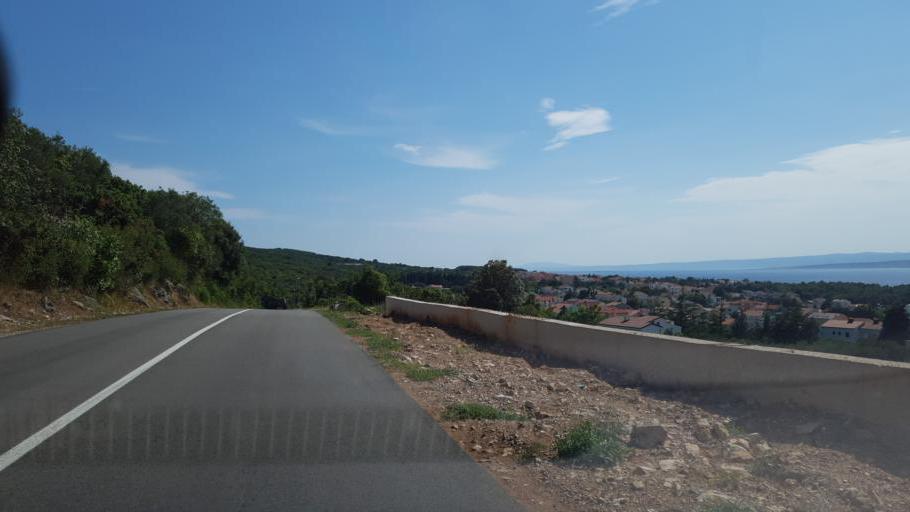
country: HR
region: Primorsko-Goranska
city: Punat
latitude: 45.0191
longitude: 14.6361
